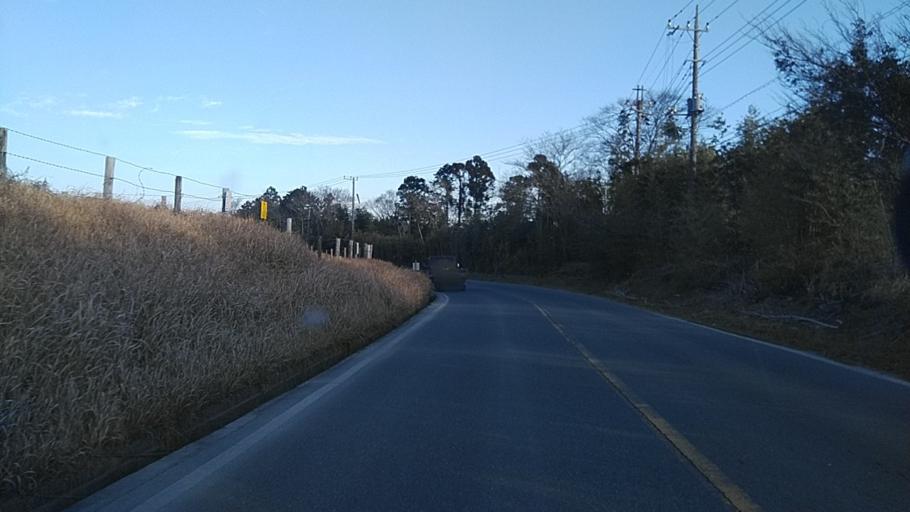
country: JP
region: Chiba
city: Kimitsu
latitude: 35.2728
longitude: 139.9896
